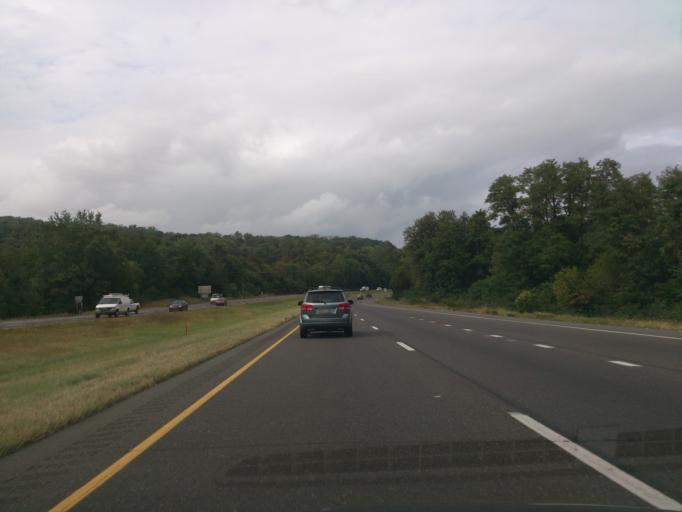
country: US
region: Pennsylvania
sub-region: Lancaster County
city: Ephrata
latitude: 40.1665
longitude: -76.1506
